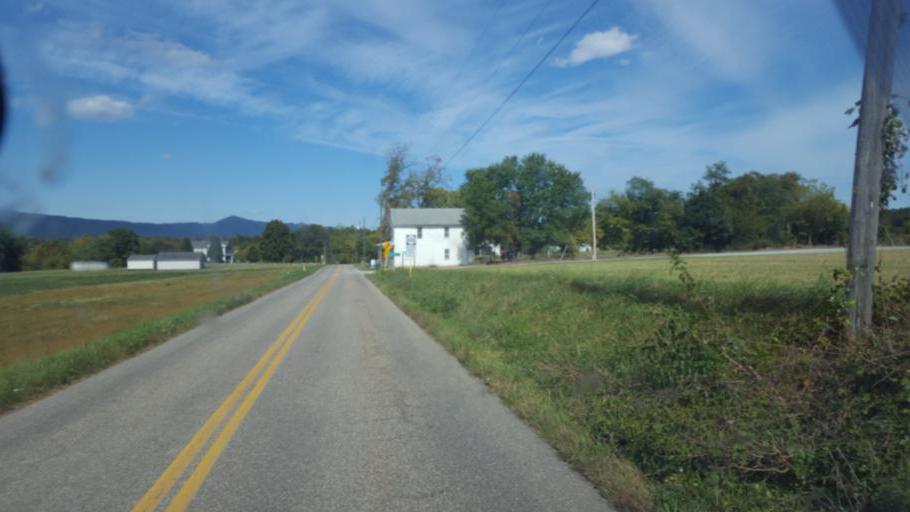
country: US
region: Virginia
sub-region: Page County
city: Stanley
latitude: 38.6240
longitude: -78.5273
